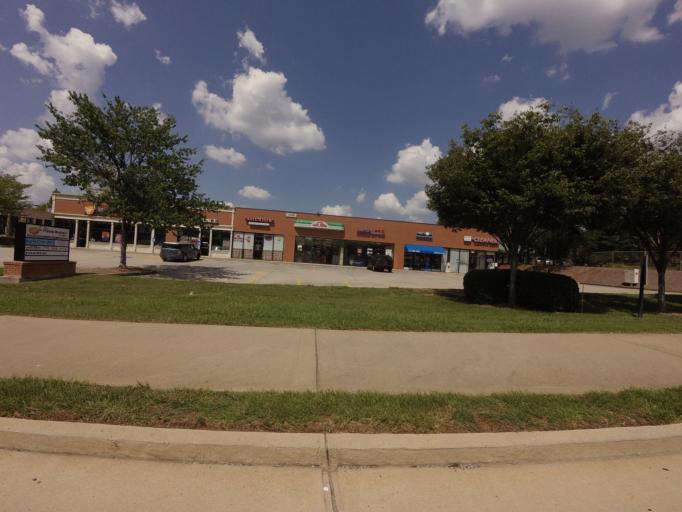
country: US
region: Georgia
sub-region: Fulton County
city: Johns Creek
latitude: 34.0498
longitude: -84.2255
